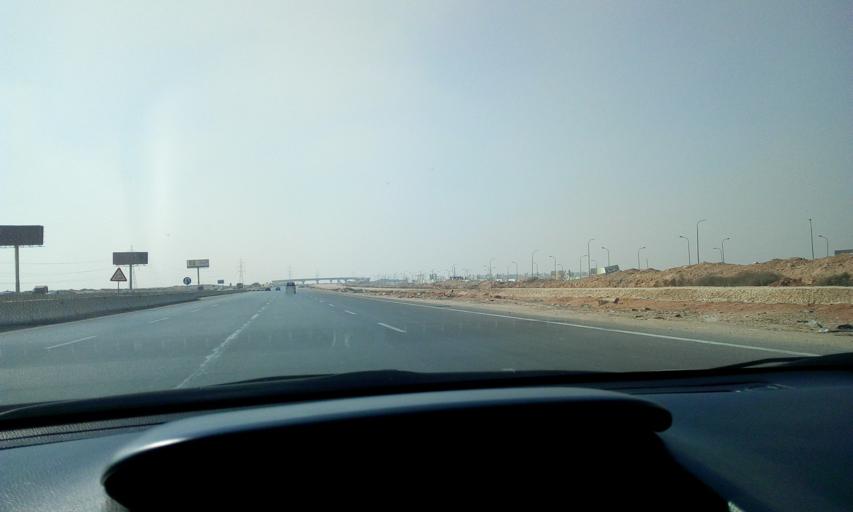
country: EG
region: Al Jizah
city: Madinat Sittah Uktubar
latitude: 29.9376
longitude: 31.0972
